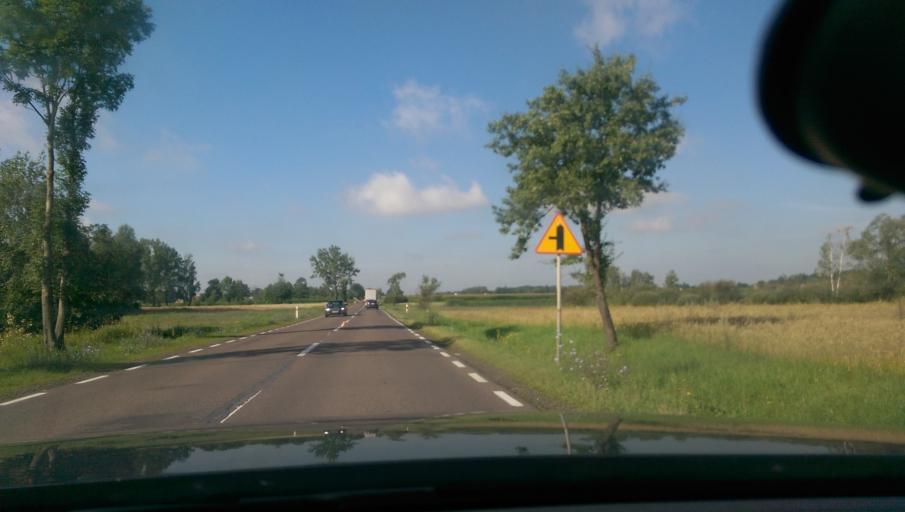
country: PL
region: Masovian Voivodeship
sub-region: Powiat plonski
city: Sochocin
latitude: 52.6666
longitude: 20.4507
